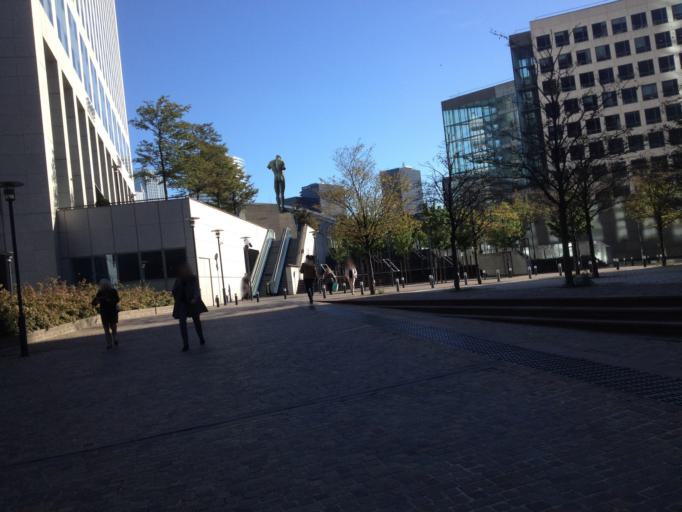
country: FR
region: Ile-de-France
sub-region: Departement des Hauts-de-Seine
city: La Defense
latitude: 48.8951
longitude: 2.2368
